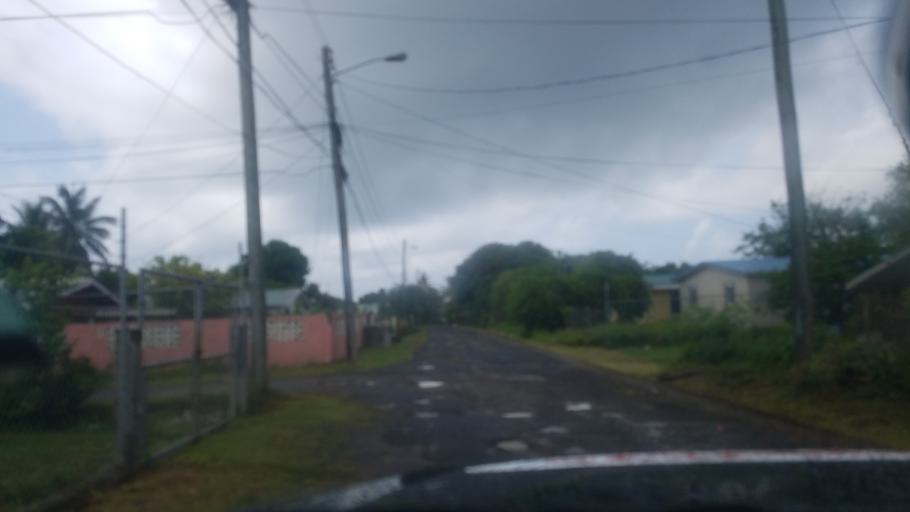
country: LC
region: Laborie Quarter
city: Laborie
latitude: 13.7467
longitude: -60.9599
